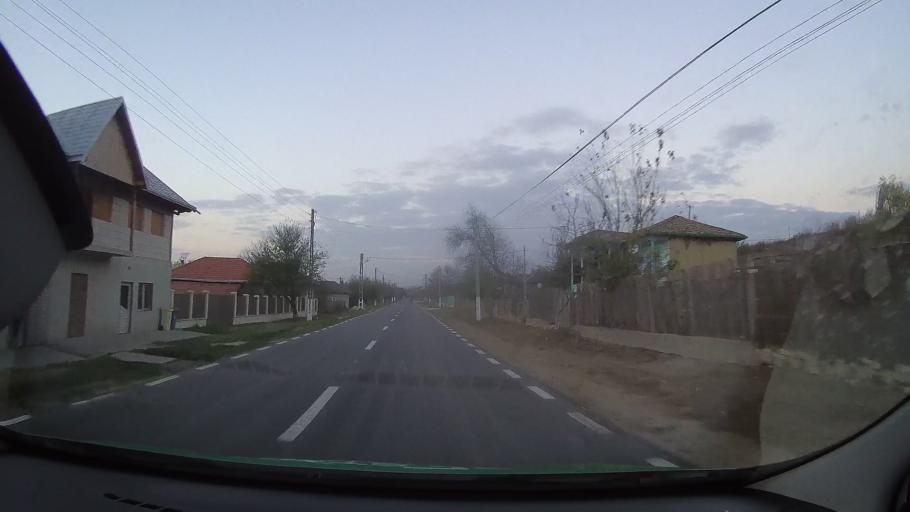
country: RO
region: Constanta
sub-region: Comuna Oltina
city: Oltina
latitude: 44.1667
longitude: 27.6667
